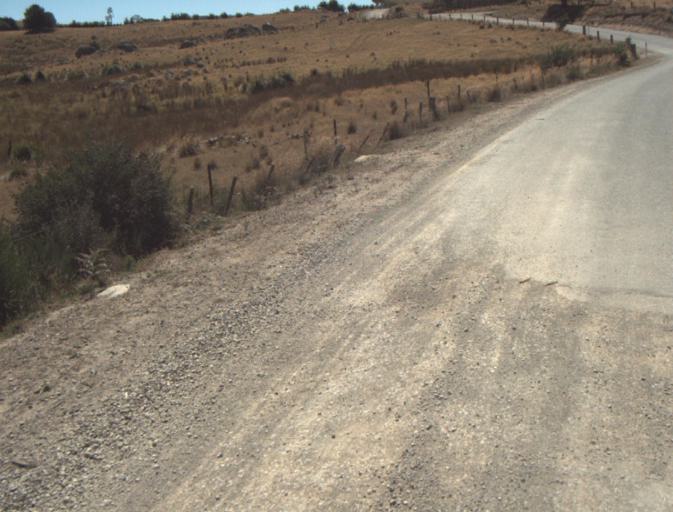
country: AU
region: Tasmania
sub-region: Dorset
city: Scottsdale
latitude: -41.3522
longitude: 147.4510
